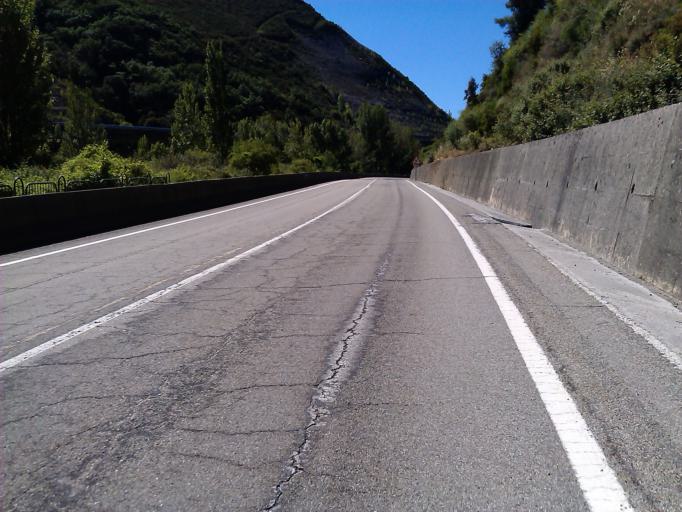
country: ES
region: Castille and Leon
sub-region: Provincia de Leon
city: Villafranca del Bierzo
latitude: 42.6175
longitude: -6.8273
